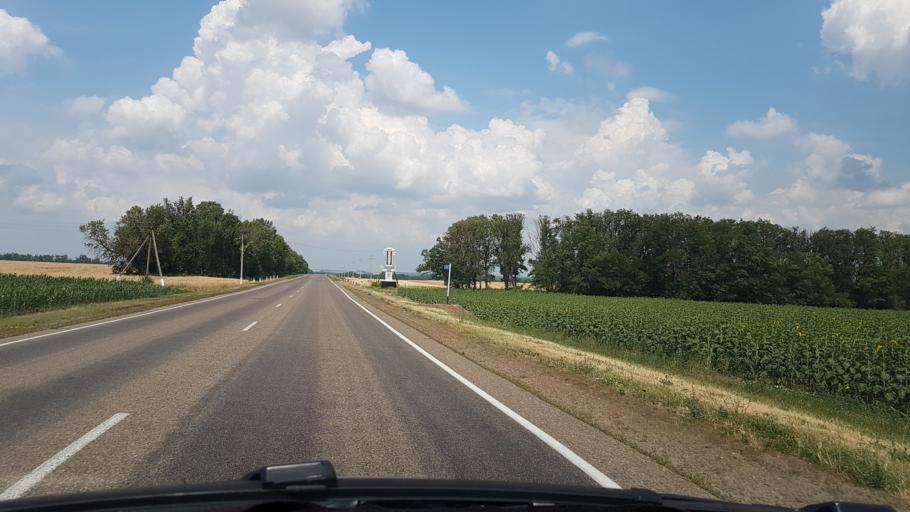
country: RU
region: Krasnodarskiy
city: Dmitriyevskaya
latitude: 45.6898
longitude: 40.7442
